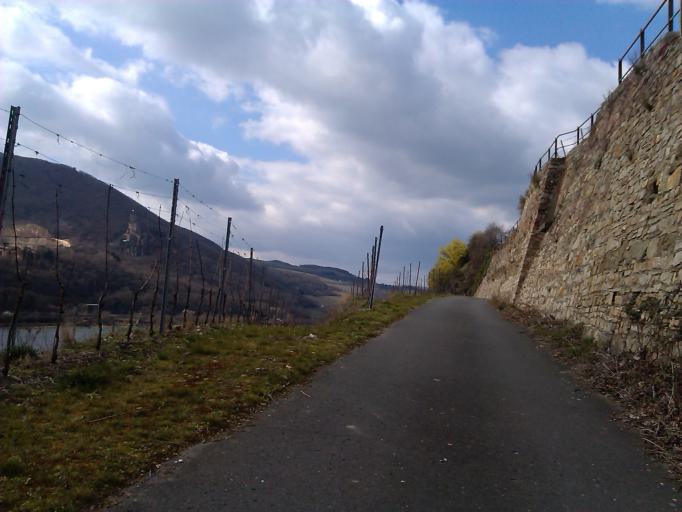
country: DE
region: Rheinland-Pfalz
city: Trechtingshausen
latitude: 50.0193
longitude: 7.8423
